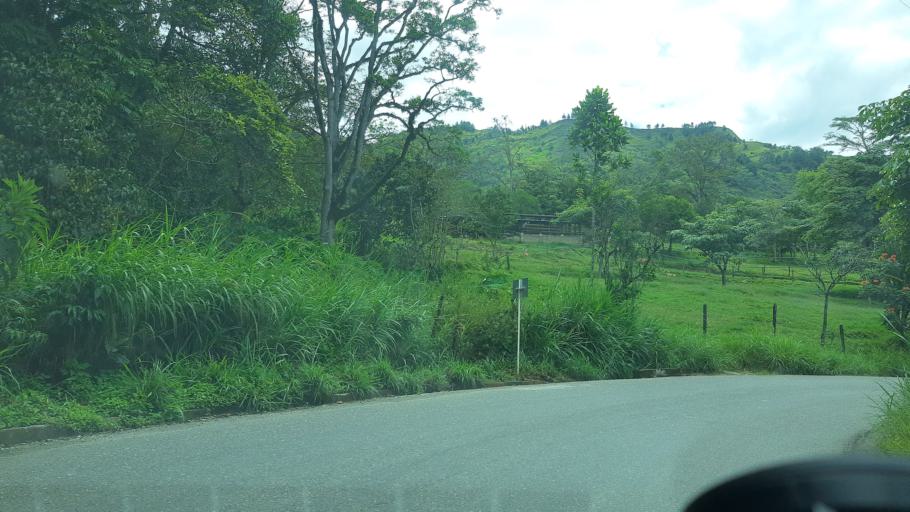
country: CO
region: Boyaca
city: Garagoa
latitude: 5.0404
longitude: -73.3877
